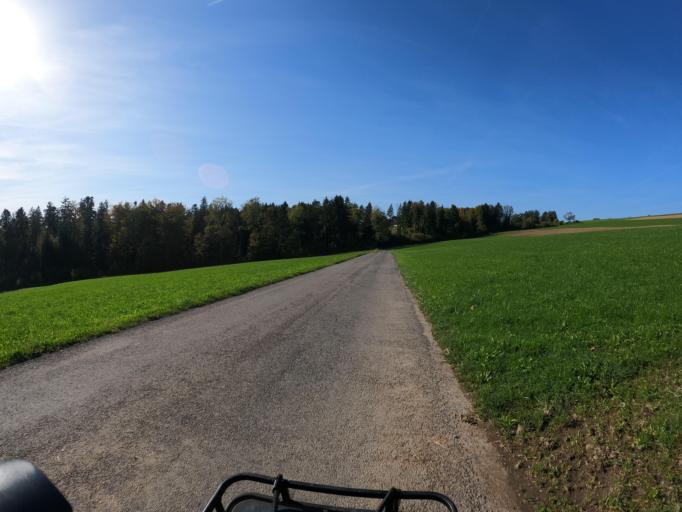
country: CH
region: Zug
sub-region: Zug
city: Baar
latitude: 47.2184
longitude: 8.5528
